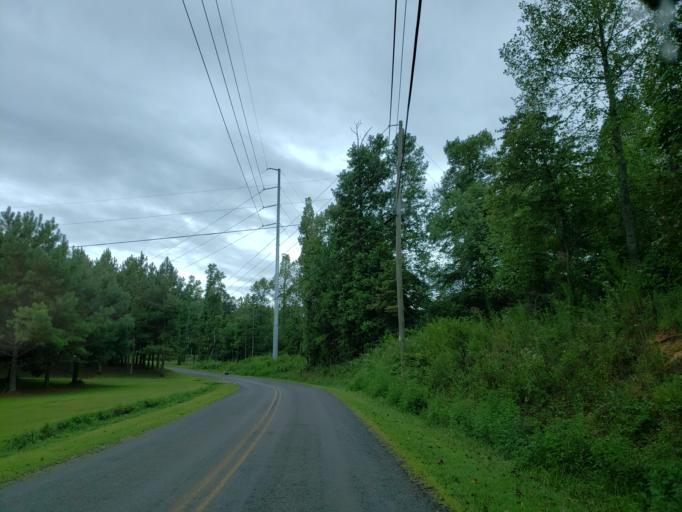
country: US
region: Georgia
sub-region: Gilmer County
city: Ellijay
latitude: 34.6083
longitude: -84.5685
